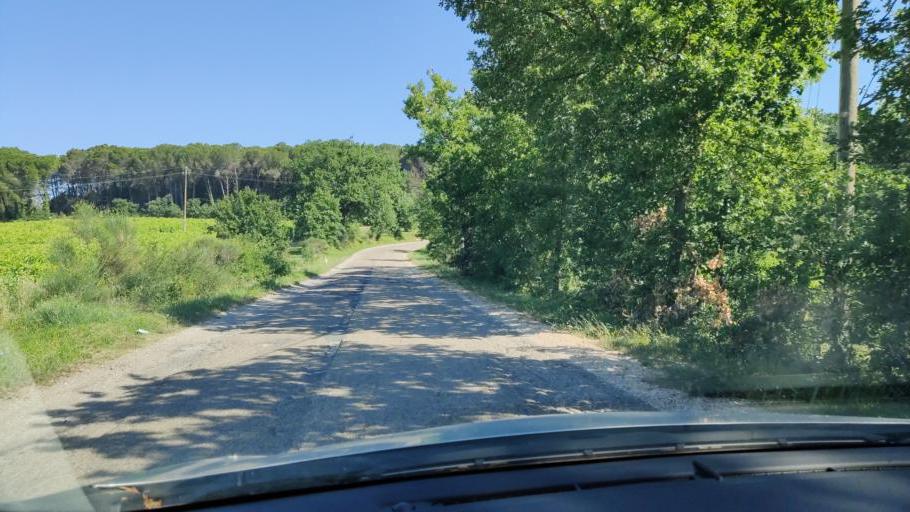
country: IT
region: Umbria
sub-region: Provincia di Terni
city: Avigliano Umbro
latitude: 42.7135
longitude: 12.4438
